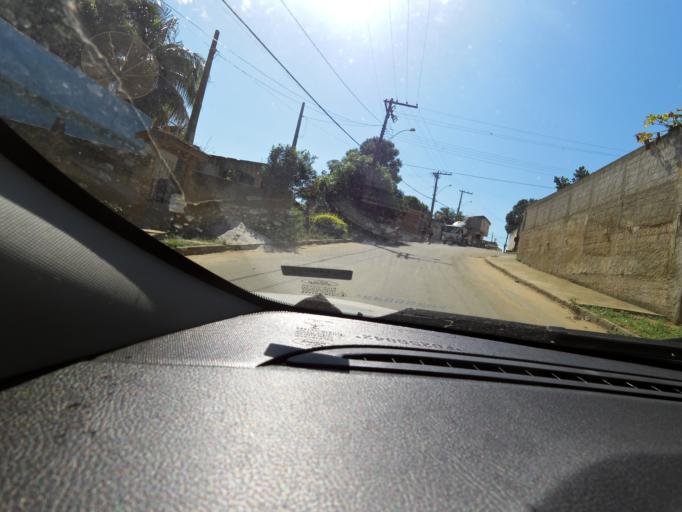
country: BR
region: Espirito Santo
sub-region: Guarapari
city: Guarapari
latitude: -20.6472
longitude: -40.5175
